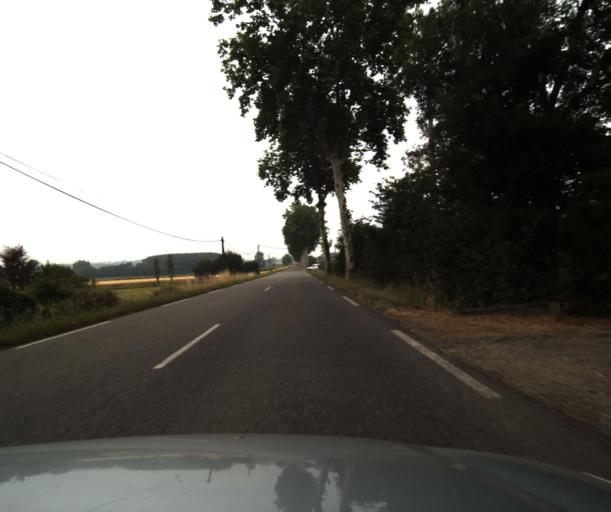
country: FR
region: Midi-Pyrenees
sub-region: Departement du Tarn-et-Garonne
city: Beaumont-de-Lomagne
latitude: 43.8400
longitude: 0.9279
